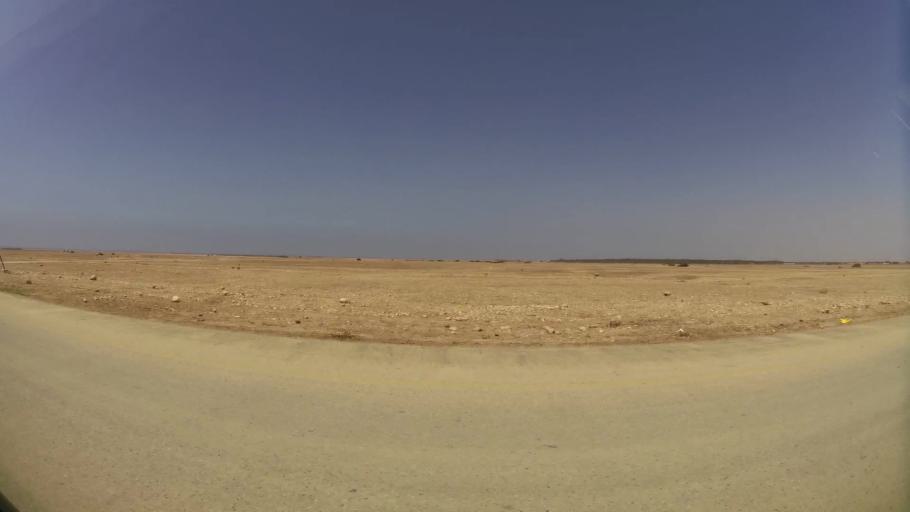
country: OM
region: Zufar
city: Salalah
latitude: 17.0466
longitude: 54.2423
